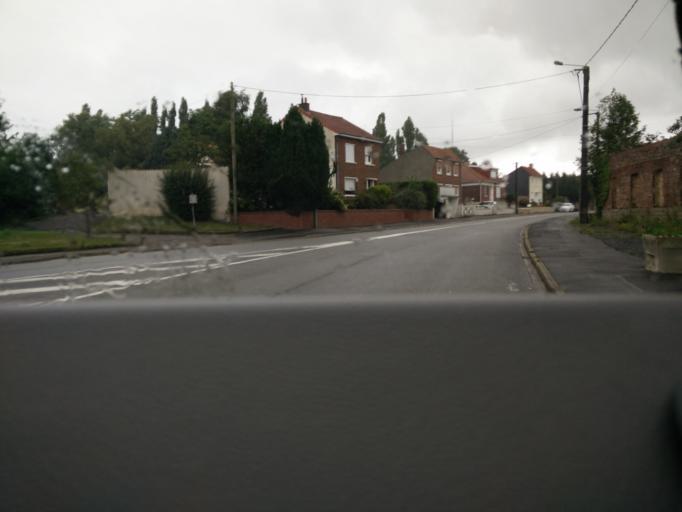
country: FR
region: Nord-Pas-de-Calais
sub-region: Departement du Pas-de-Calais
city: Bouvigny-Boyeffles
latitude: 50.4078
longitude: 2.6350
